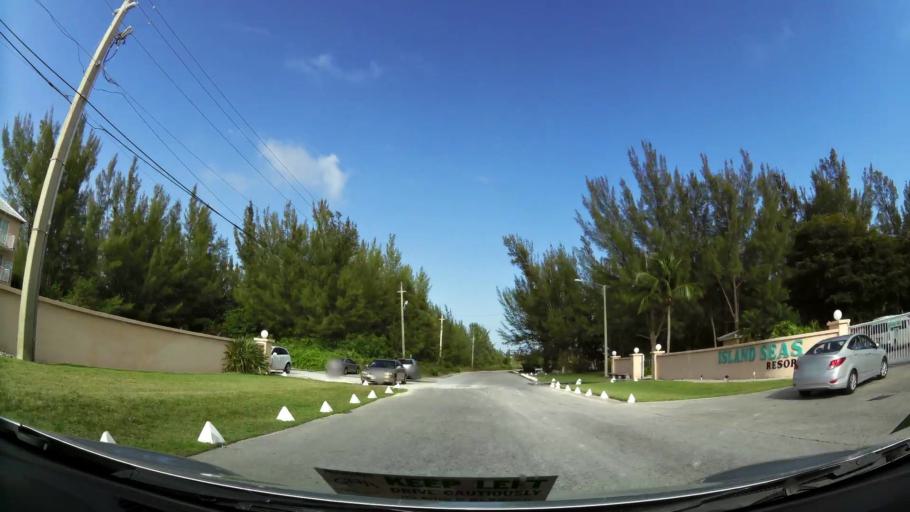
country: BS
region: Freeport
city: Lucaya
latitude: 26.4987
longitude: -78.6678
